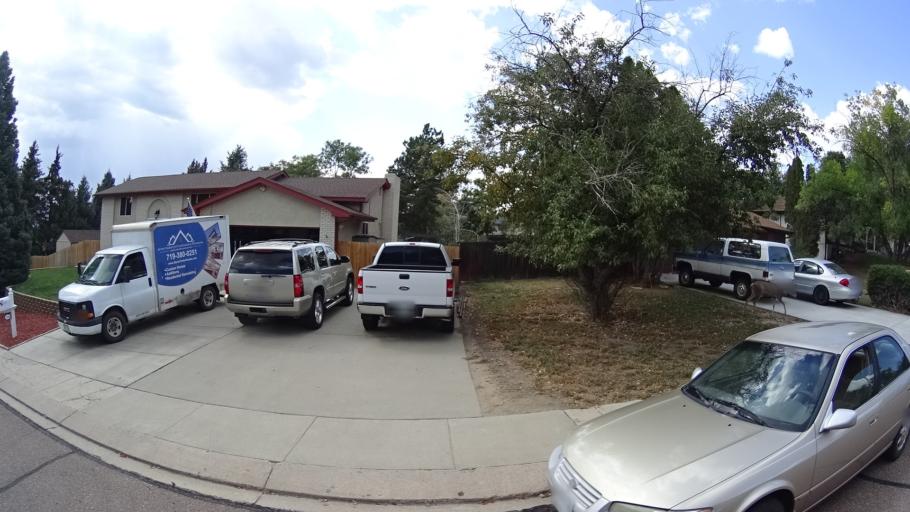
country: US
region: Colorado
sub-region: El Paso County
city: Cimarron Hills
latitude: 38.8712
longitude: -104.7280
